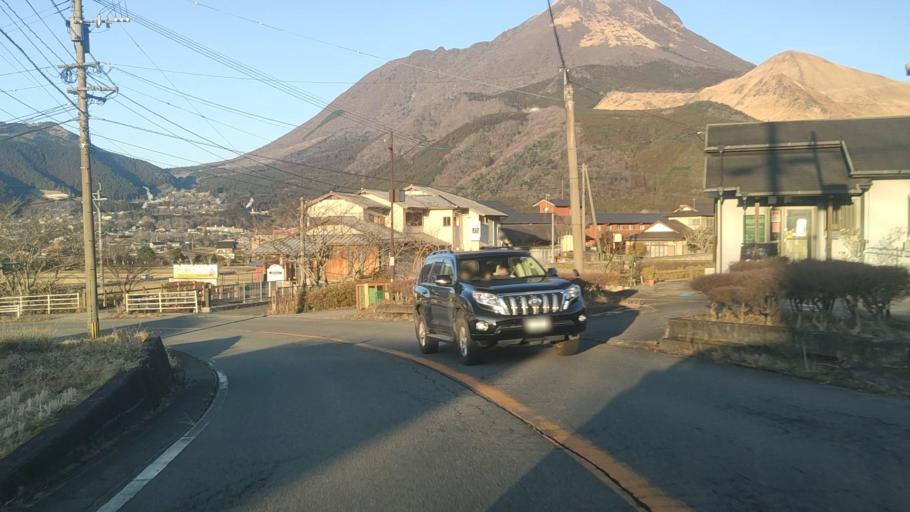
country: JP
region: Oita
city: Beppu
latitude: 33.2559
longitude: 131.3595
